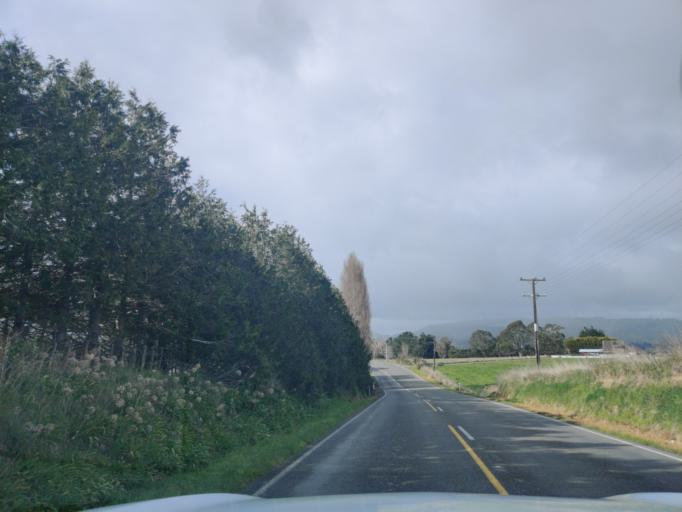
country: NZ
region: Manawatu-Wanganui
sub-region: Palmerston North City
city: Palmerston North
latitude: -40.2947
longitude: 175.7361
